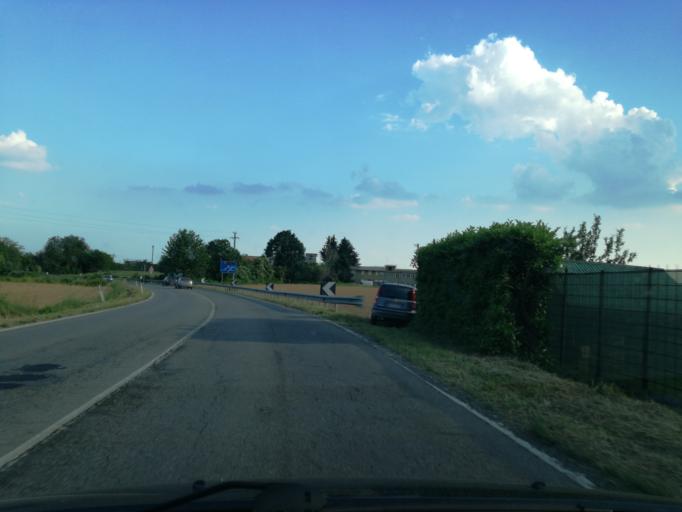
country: IT
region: Lombardy
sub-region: Provincia di Monza e Brianza
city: Cornate d'Adda
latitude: 45.6267
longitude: 9.4643
